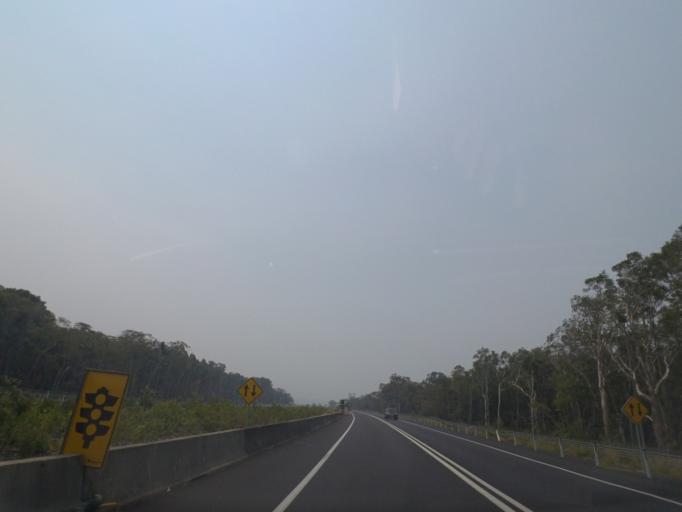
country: AU
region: New South Wales
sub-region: Ballina
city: Ballina
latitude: -28.9134
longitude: 153.4784
